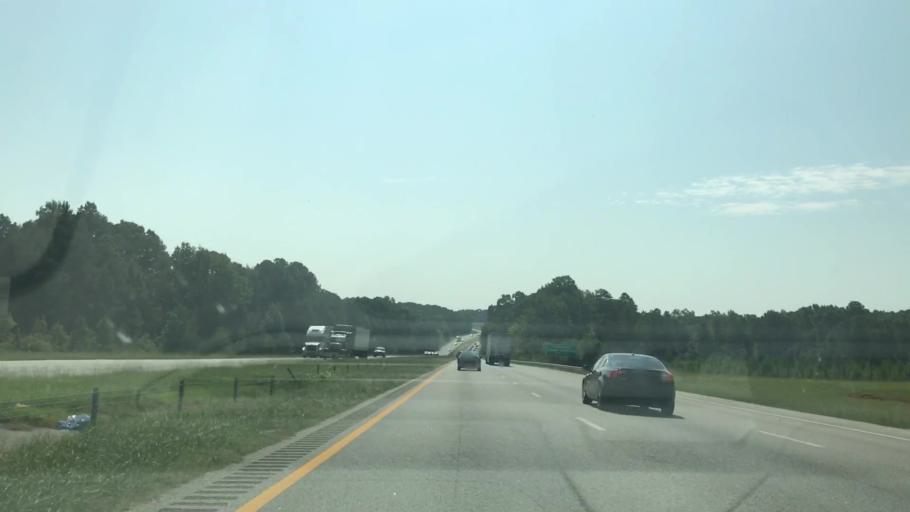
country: US
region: South Carolina
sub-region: Laurens County
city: Clinton
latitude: 34.5043
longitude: -81.8548
